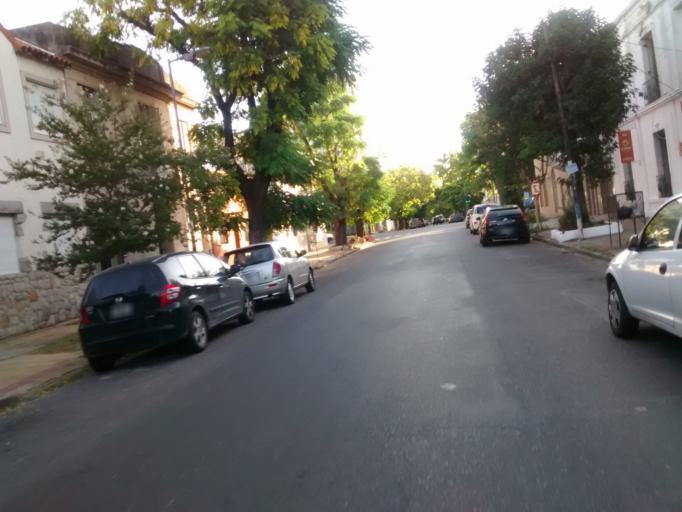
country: AR
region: Buenos Aires
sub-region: Partido de La Plata
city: La Plata
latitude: -34.9238
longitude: -57.9365
